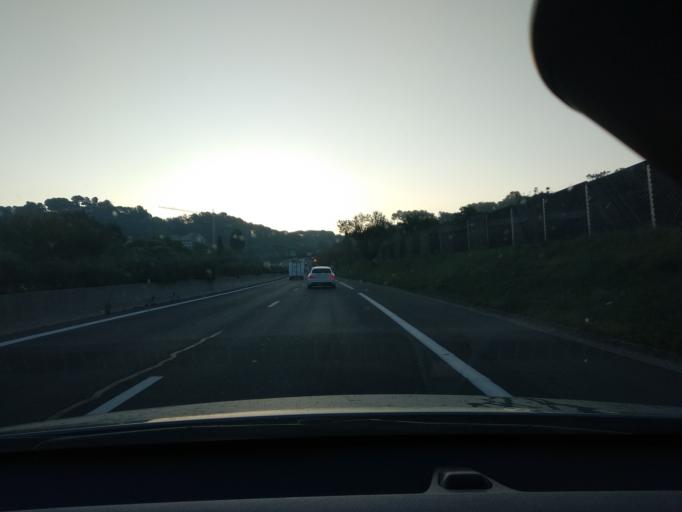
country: FR
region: Provence-Alpes-Cote d'Azur
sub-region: Departement des Alpes-Maritimes
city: Mouans-Sartoux
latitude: 43.6077
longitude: 6.9790
